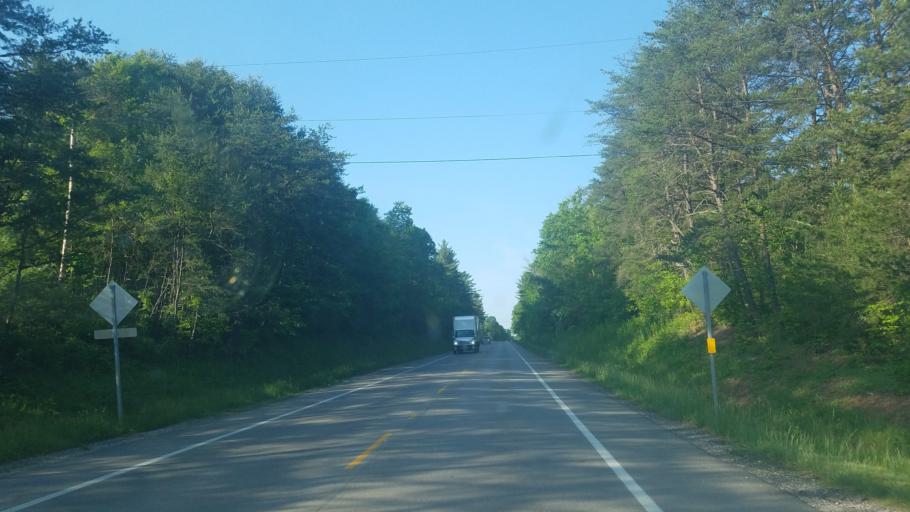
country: US
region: West Virginia
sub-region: Mason County
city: New Haven
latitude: 39.1454
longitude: -81.8537
